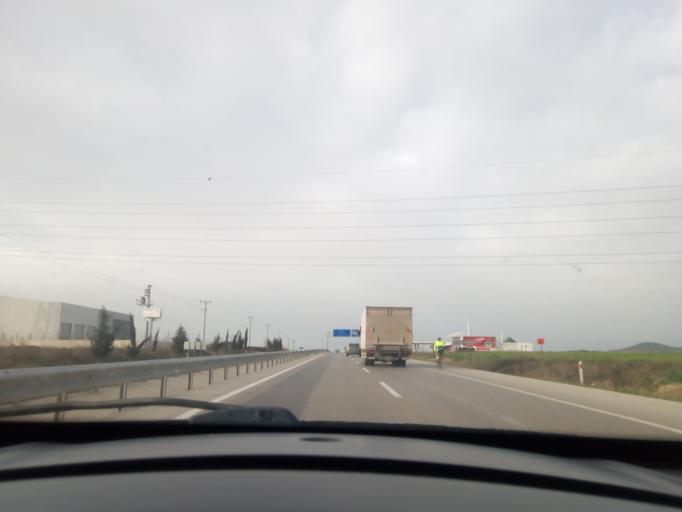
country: TR
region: Bursa
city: Gorukle
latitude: 40.2183
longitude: 28.7592
